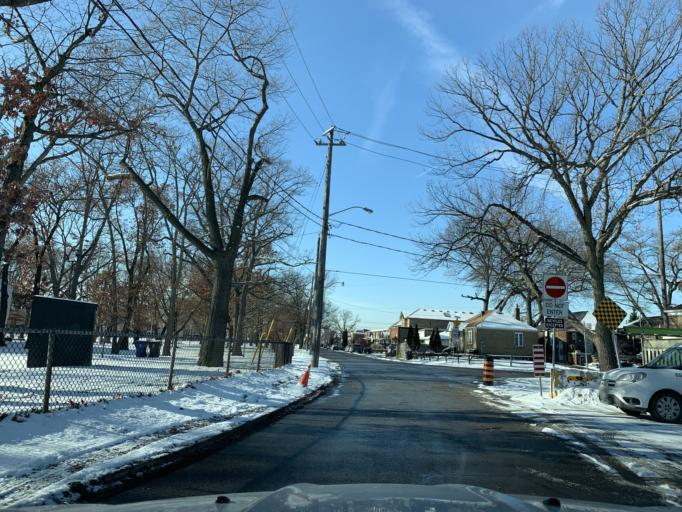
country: CA
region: Ontario
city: Toronto
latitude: 43.6692
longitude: -79.4771
